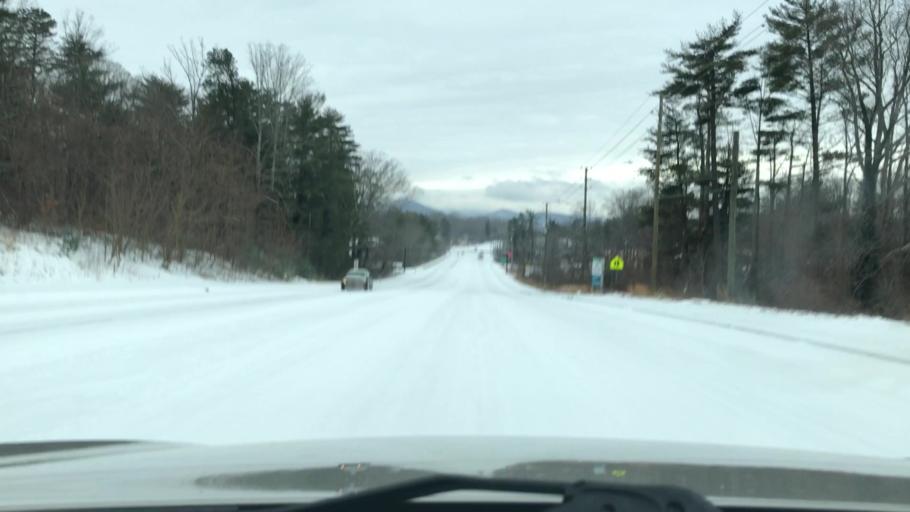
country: US
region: North Carolina
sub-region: Buncombe County
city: Royal Pines
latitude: 35.4844
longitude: -82.5291
